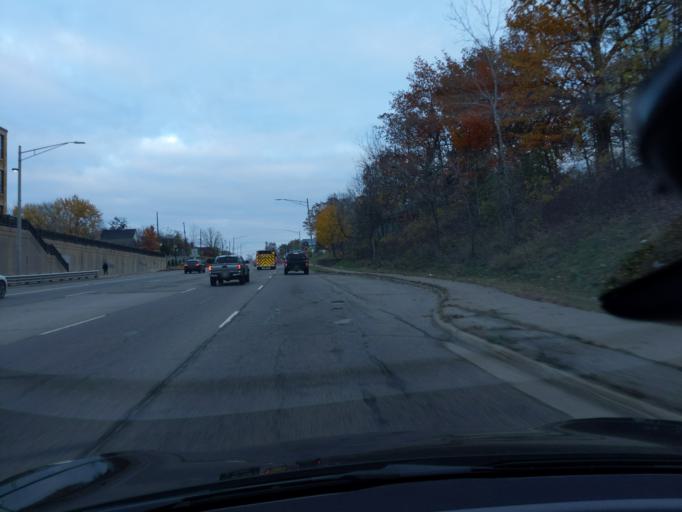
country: US
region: Michigan
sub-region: Ingham County
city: Lansing
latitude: 42.7406
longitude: -84.5421
